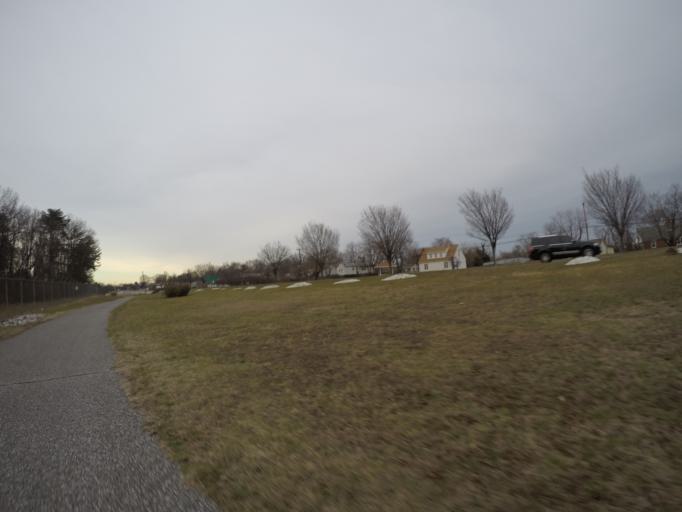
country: US
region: Maryland
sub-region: Anne Arundel County
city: Ferndale
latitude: 39.1847
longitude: -76.6532
